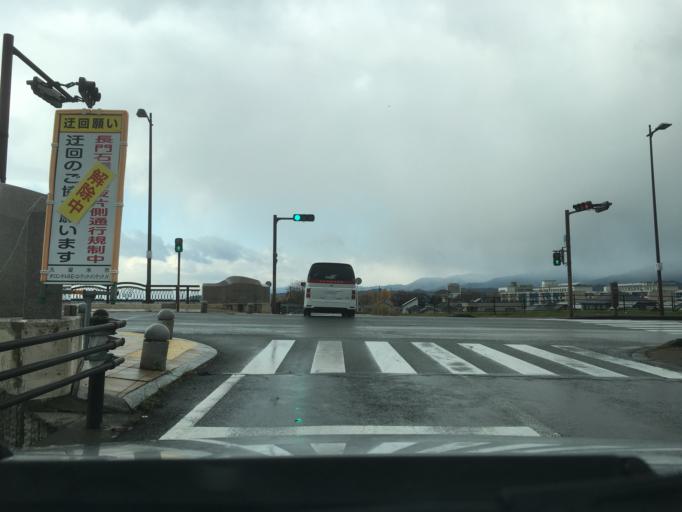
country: JP
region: Fukuoka
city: Kurume
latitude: 33.3337
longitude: 130.5148
